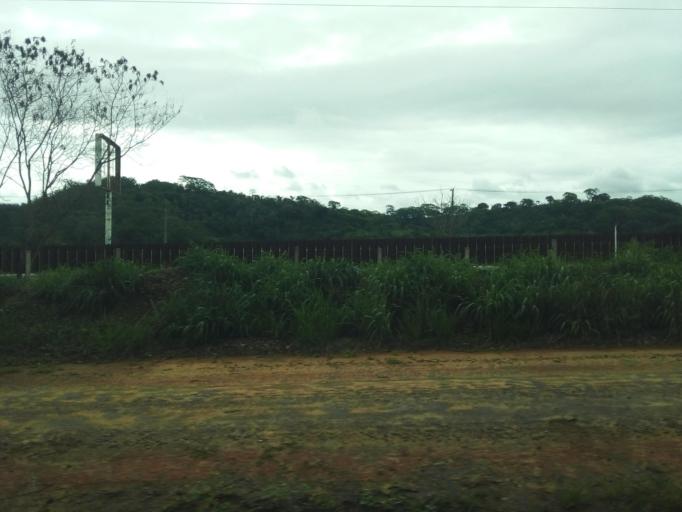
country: BR
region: Minas Gerais
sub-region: Ipatinga
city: Ipatinga
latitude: -19.4799
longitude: -42.4905
